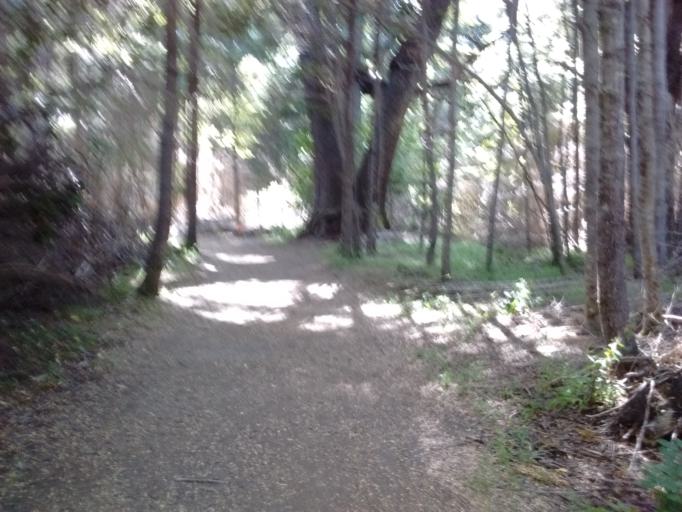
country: AR
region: Rio Negro
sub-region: Departamento de Bariloche
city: San Carlos de Bariloche
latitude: -41.0627
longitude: -71.5671
